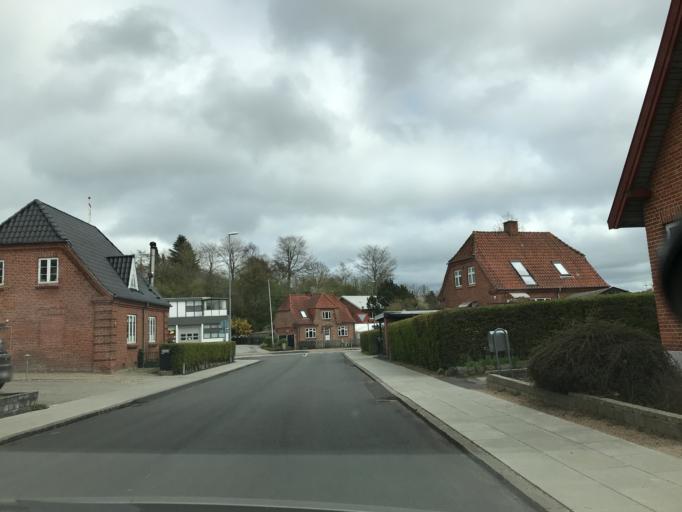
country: DK
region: Central Jutland
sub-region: Skive Kommune
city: Skive
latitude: 56.5780
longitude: 9.0277
